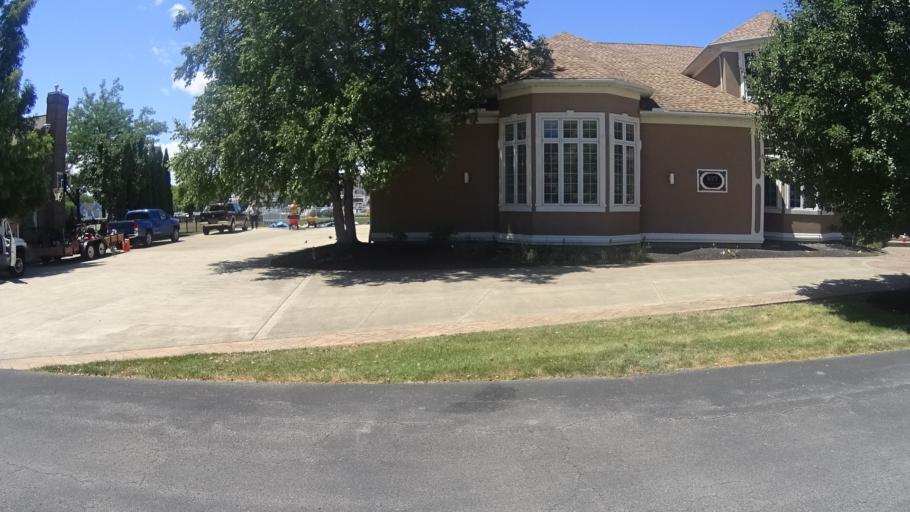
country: US
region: Ohio
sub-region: Erie County
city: Sandusky
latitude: 41.4446
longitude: -82.6712
